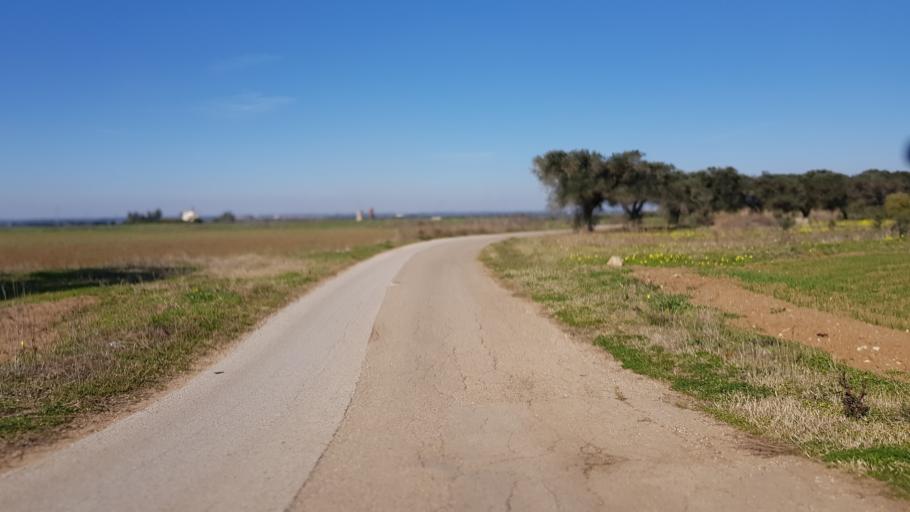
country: IT
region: Apulia
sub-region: Provincia di Brindisi
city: Mesagne
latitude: 40.6211
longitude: 17.8284
